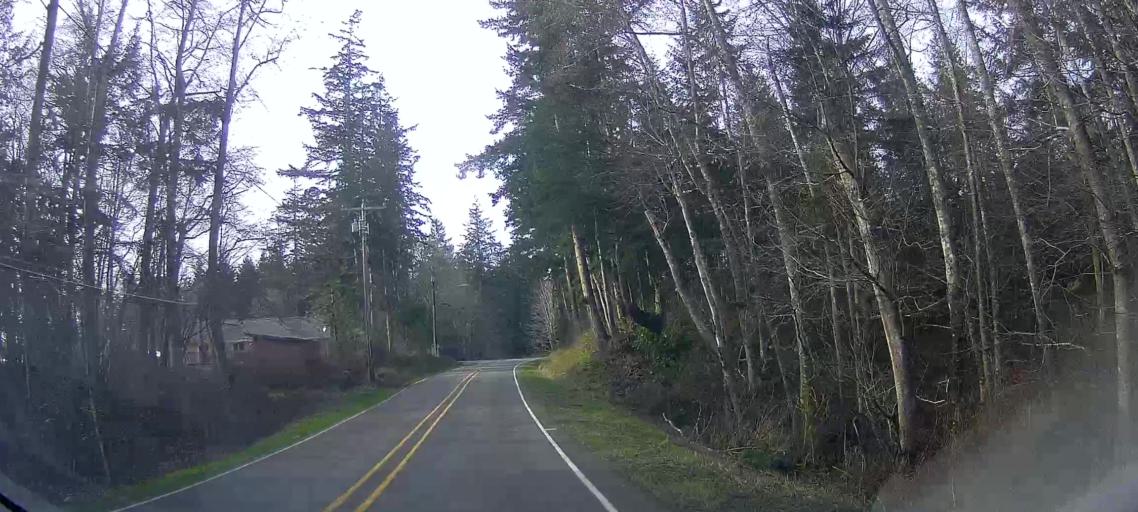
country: US
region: Washington
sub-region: Island County
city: Camano
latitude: 48.1392
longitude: -122.5035
